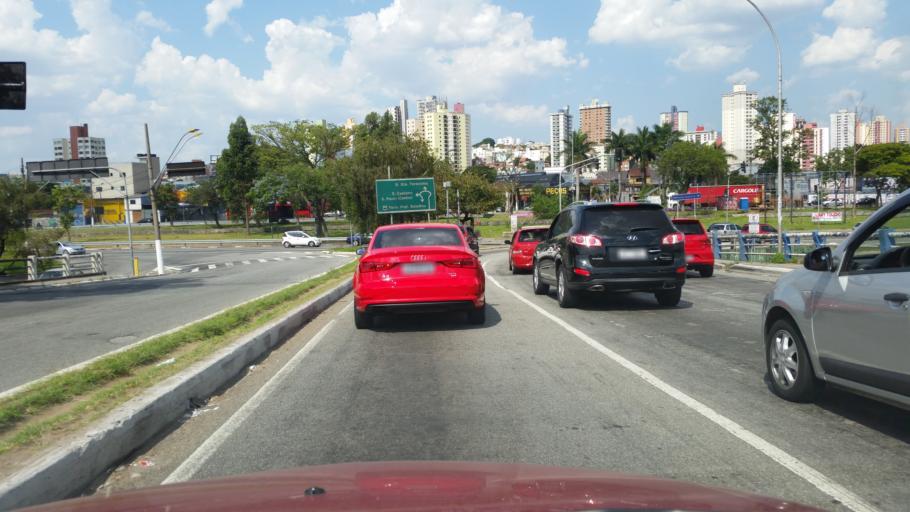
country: BR
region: Sao Paulo
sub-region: Sao Caetano Do Sul
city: Sao Caetano do Sul
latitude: -23.6385
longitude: -46.5356
